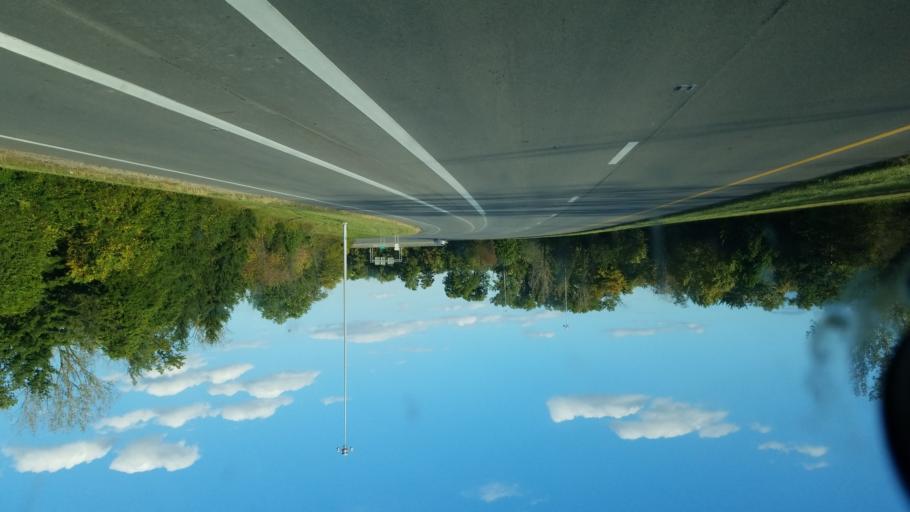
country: US
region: Ohio
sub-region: Franklin County
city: Gahanna
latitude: 40.0154
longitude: -82.9008
